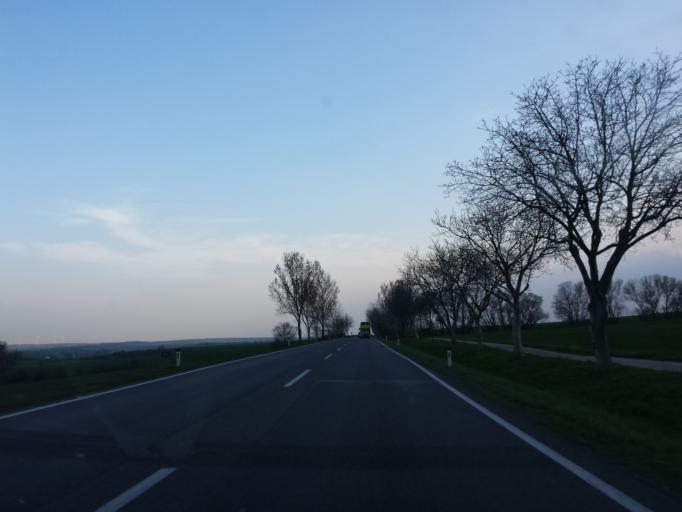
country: AT
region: Lower Austria
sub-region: Politischer Bezirk Mistelbach
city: Wilfersdorf
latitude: 48.6156
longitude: 16.6478
